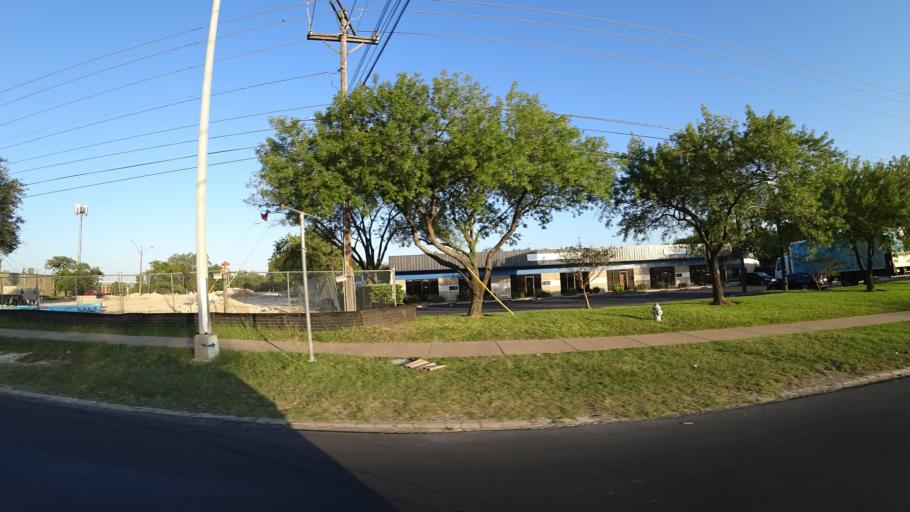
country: US
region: Texas
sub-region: Travis County
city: Austin
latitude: 30.3509
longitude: -97.7092
